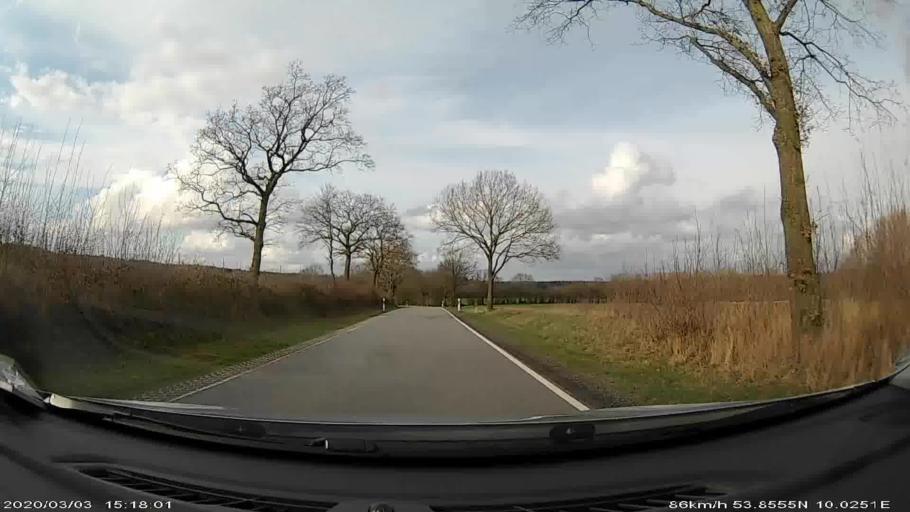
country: DE
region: Schleswig-Holstein
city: Kattendorf
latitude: 53.8549
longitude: 10.0254
